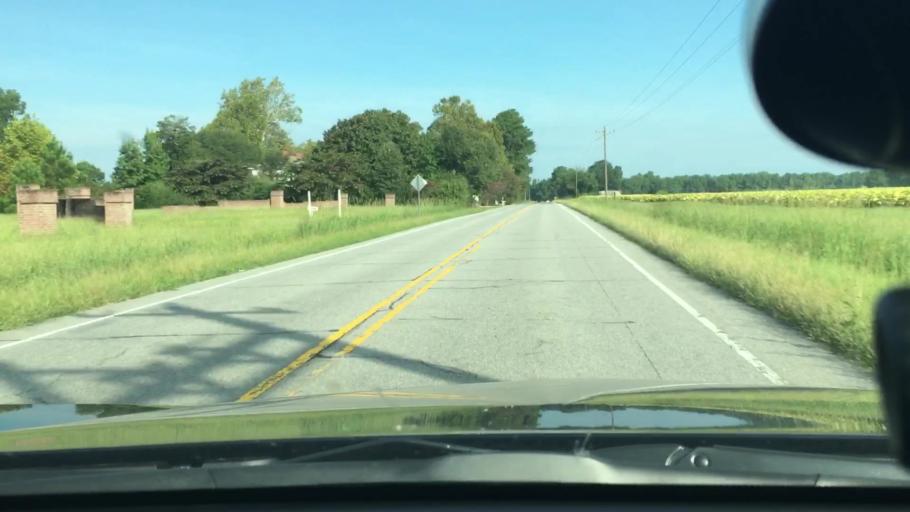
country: US
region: North Carolina
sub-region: Edgecombe County
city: Pinetops
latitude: 35.7481
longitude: -77.5425
